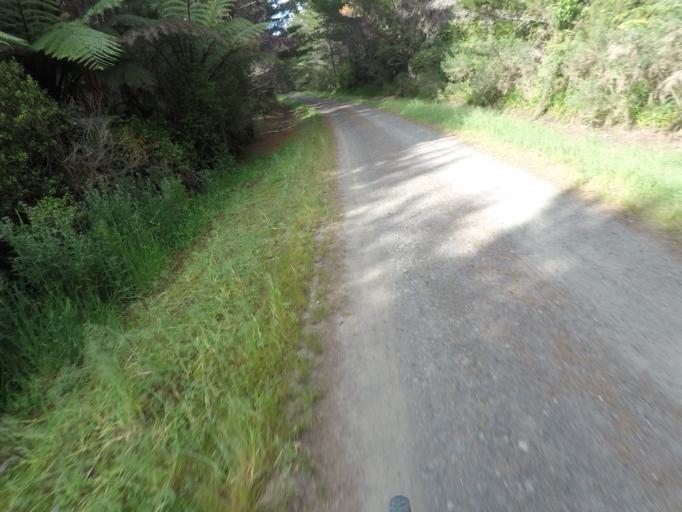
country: NZ
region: Auckland
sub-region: Auckland
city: Muriwai Beach
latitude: -36.7446
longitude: 174.5656
